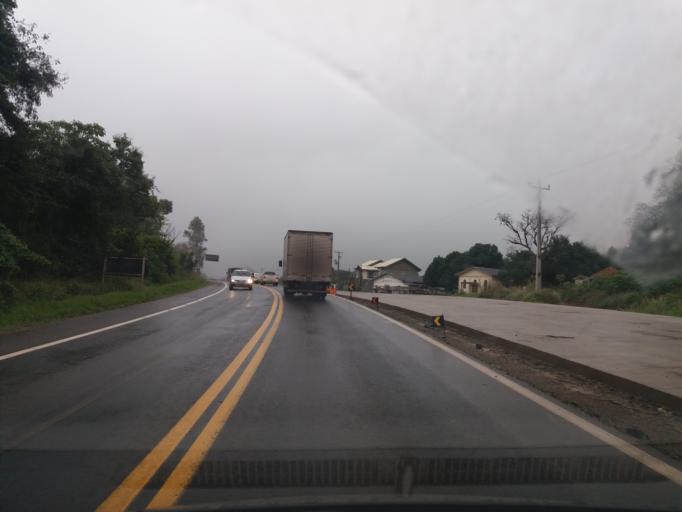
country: BR
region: Parana
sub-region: Realeza
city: Realeza
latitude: -25.4674
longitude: -53.5815
